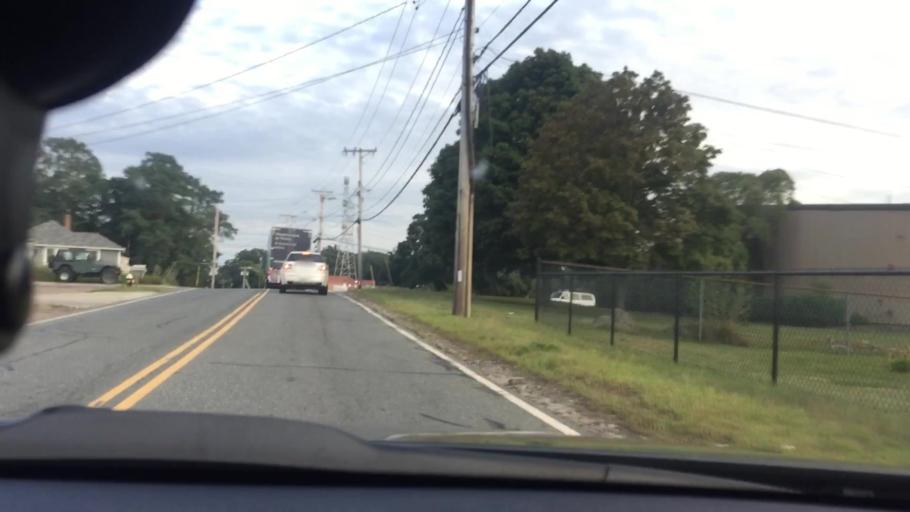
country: US
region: Massachusetts
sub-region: Norfolk County
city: Randolph
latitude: 42.1471
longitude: -71.0709
